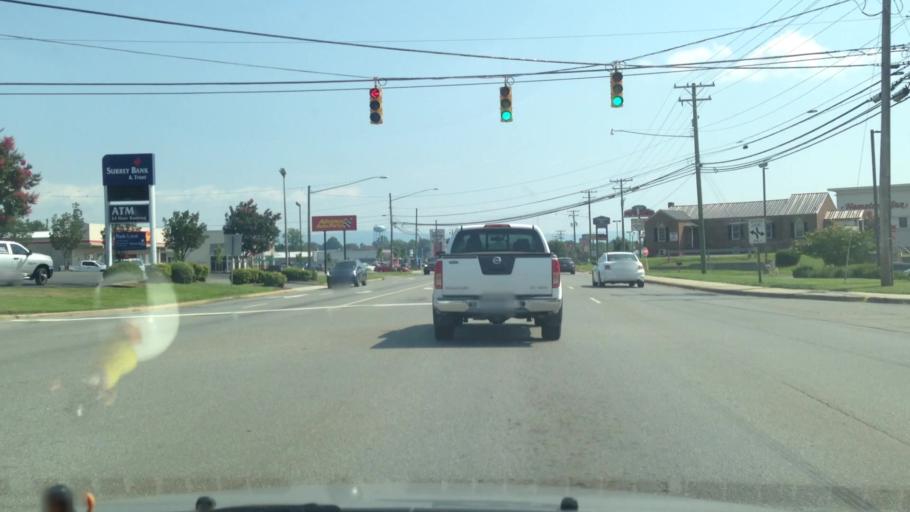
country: US
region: North Carolina
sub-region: Surry County
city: Mount Airy
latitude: 36.4785
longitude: -80.6171
